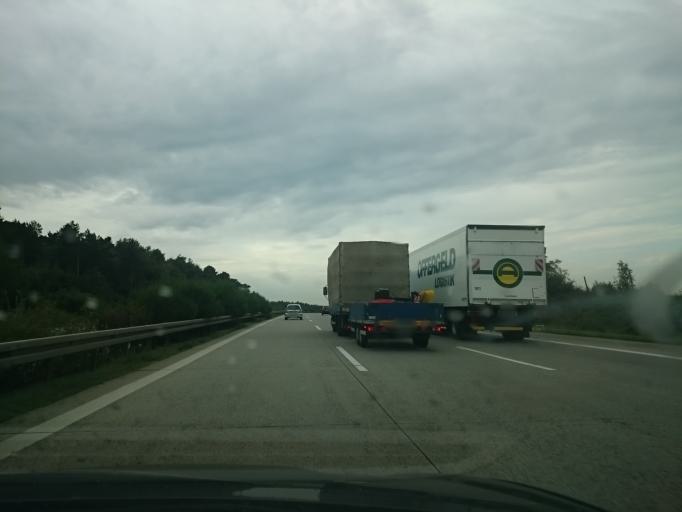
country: DE
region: Brandenburg
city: Linthe
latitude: 52.1261
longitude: 12.7447
